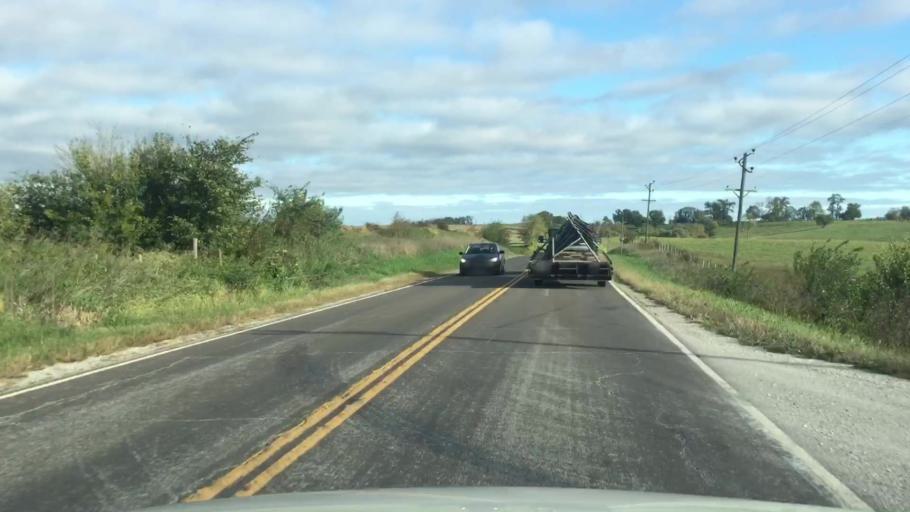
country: US
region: Missouri
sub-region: Howard County
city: New Franklin
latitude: 39.0760
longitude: -92.7457
